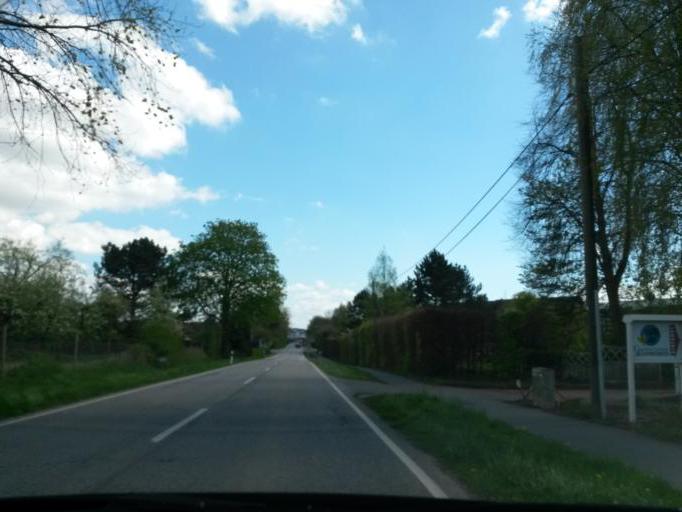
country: DE
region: Schleswig-Holstein
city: Wedel
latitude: 53.5928
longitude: 9.6852
